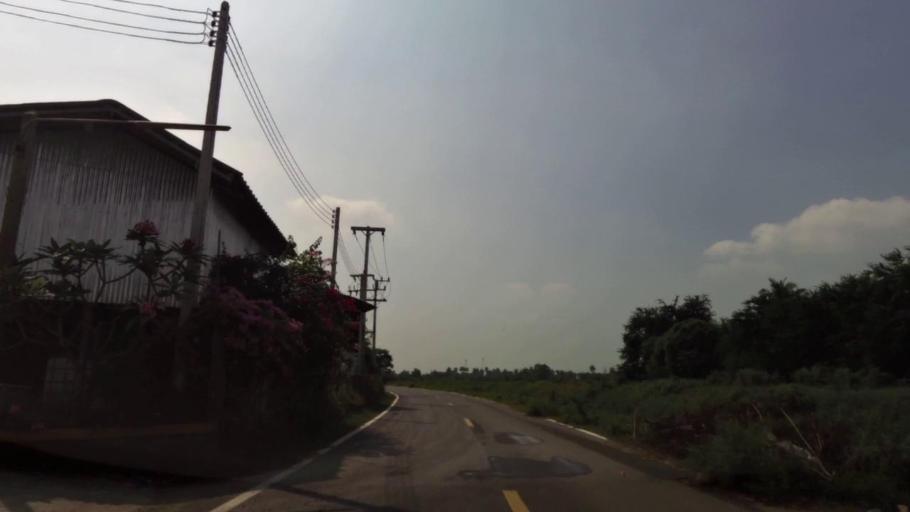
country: TH
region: Ang Thong
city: Pho Thong
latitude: 14.6121
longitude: 100.3983
